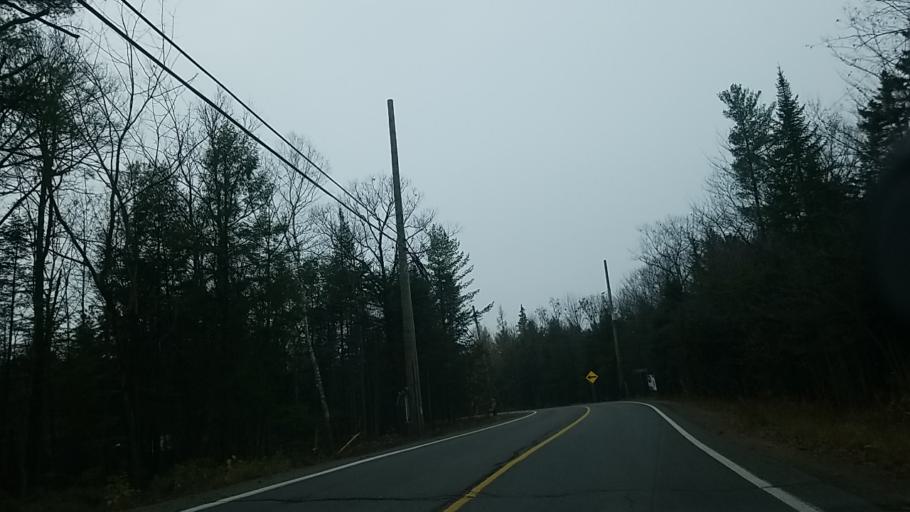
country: CA
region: Quebec
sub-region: Laurentides
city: Saint-Colomban
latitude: 45.7878
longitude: -74.1221
